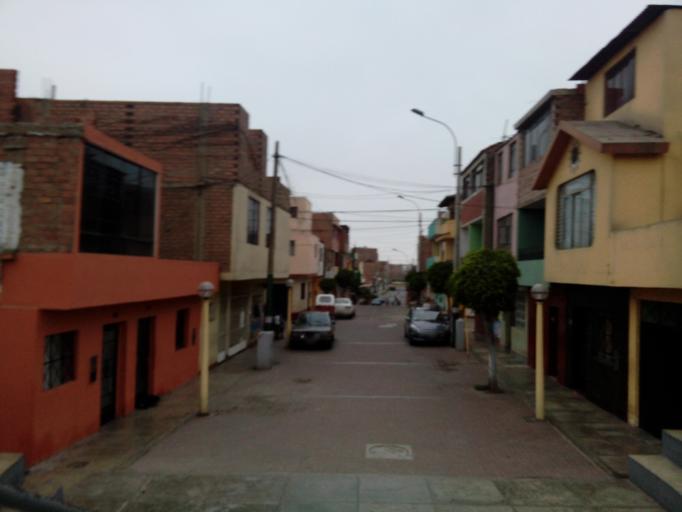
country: PE
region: Callao
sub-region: Callao
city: Callao
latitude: -12.0398
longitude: -77.0857
